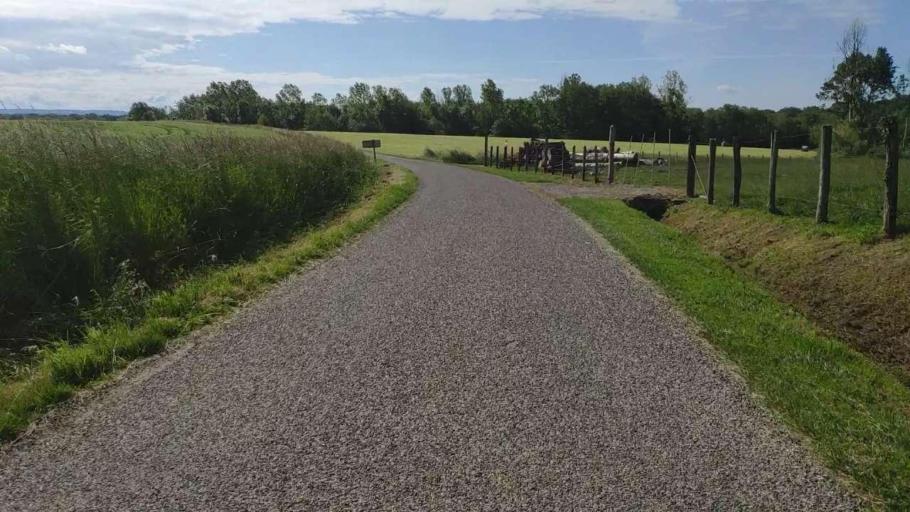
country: FR
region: Franche-Comte
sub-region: Departement du Jura
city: Bletterans
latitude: 46.7066
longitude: 5.4646
